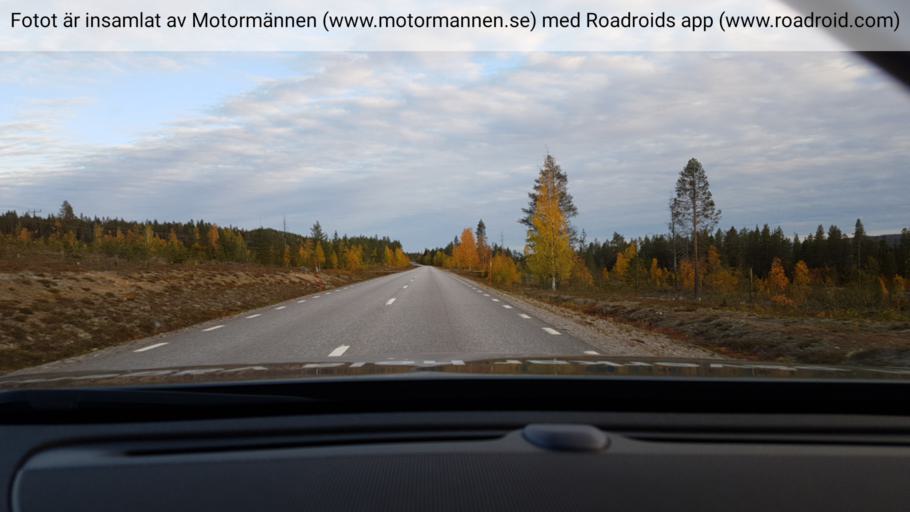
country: SE
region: Norrbotten
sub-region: Jokkmokks Kommun
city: Jokkmokk
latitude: 66.3863
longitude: 19.7104
